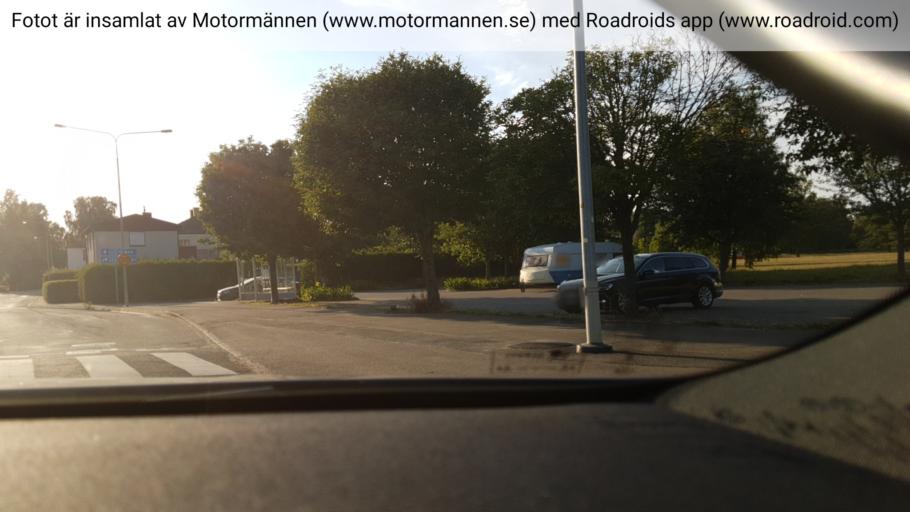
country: SE
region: Vaestra Goetaland
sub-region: Skara Kommun
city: Axvall
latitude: 58.3883
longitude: 13.5757
